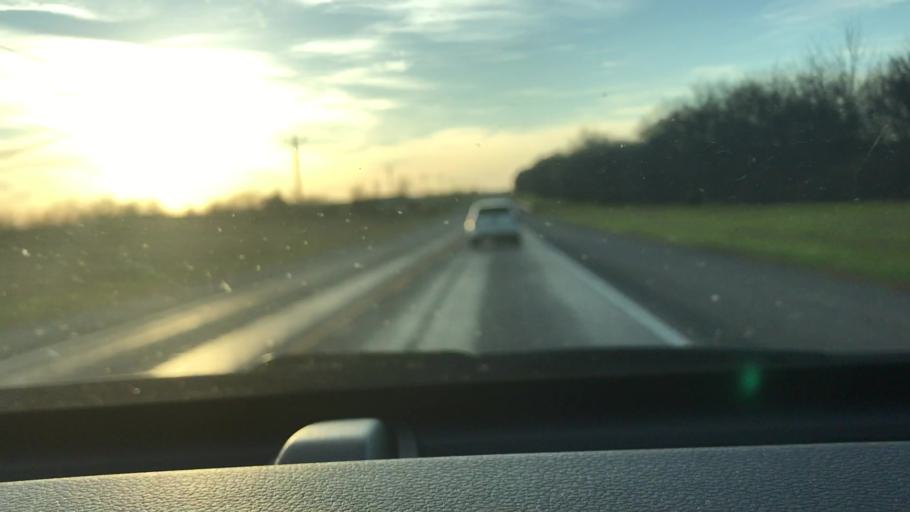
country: US
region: Texas
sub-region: Red River County
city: Clarksville
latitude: 33.6069
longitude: -95.0055
